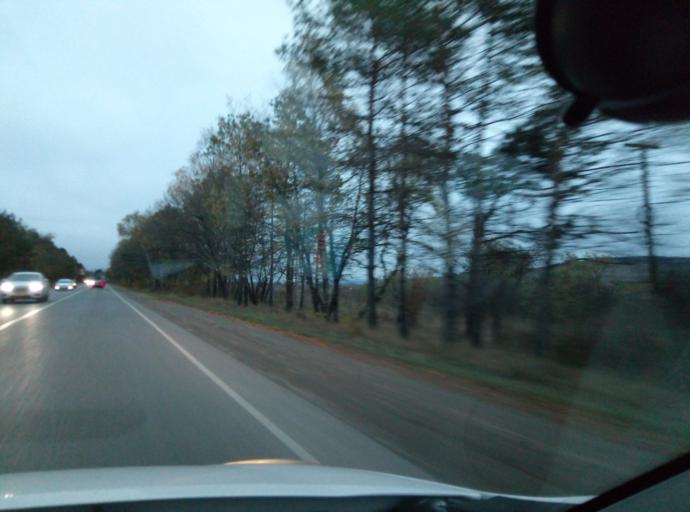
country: RU
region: Stavropol'skiy
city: Vinsady
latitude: 44.0546
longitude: 42.9263
